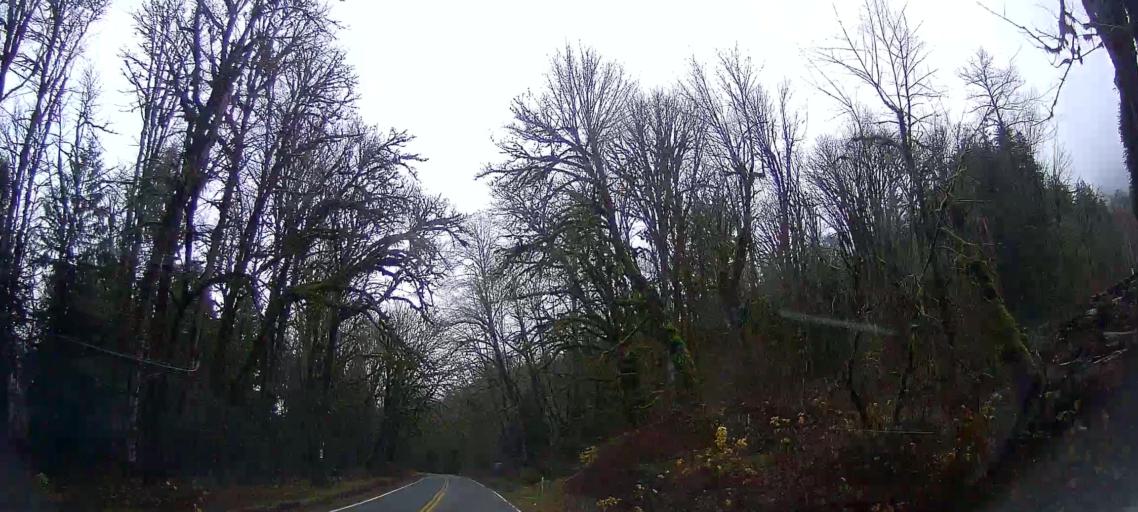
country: US
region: Washington
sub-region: Skagit County
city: Sedro-Woolley
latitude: 48.5088
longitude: -121.8944
